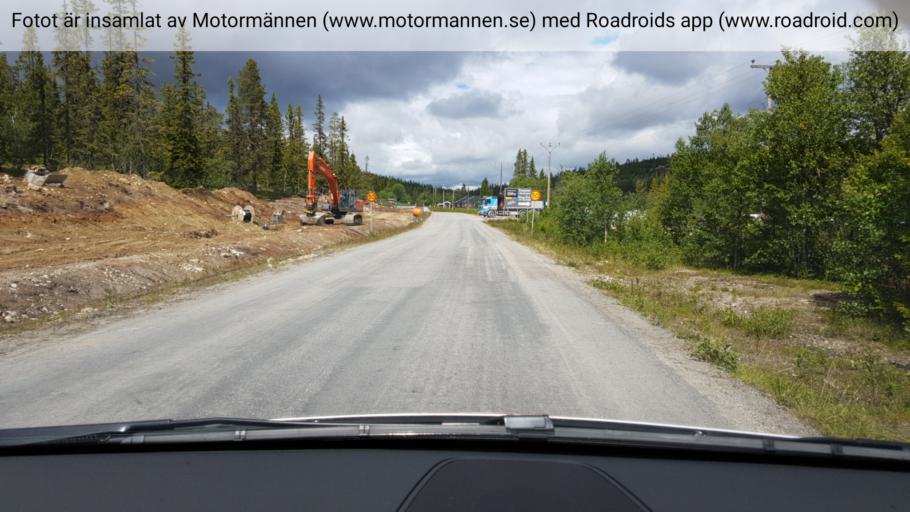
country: SE
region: Jaemtland
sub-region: Bergs Kommun
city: Hoverberg
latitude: 62.4989
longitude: 14.1103
